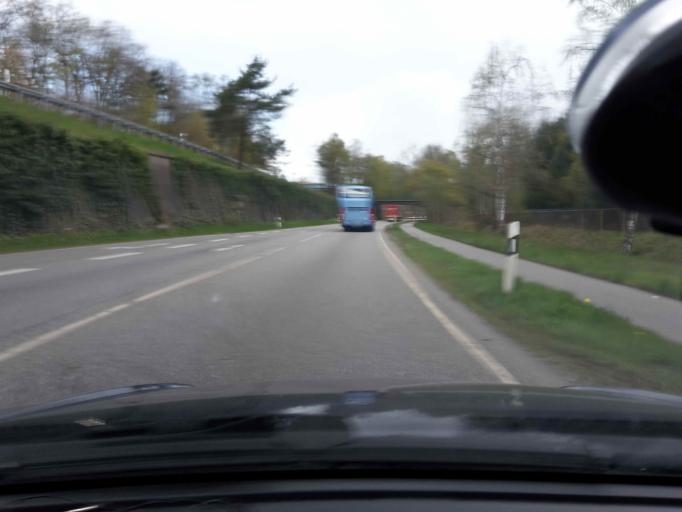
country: DE
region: Lower Saxony
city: Buxtehude
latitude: 53.4655
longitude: 9.6802
